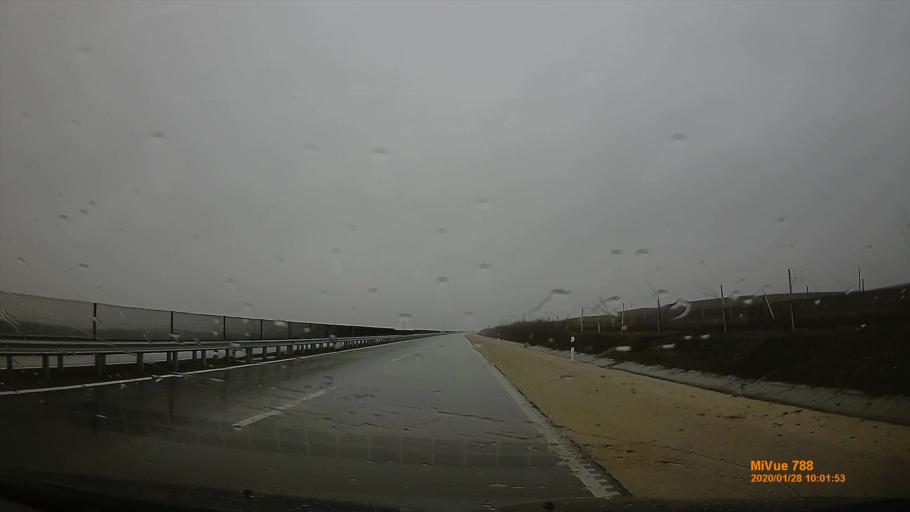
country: HU
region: Pest
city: Albertirsa
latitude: 47.2740
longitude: 19.6000
